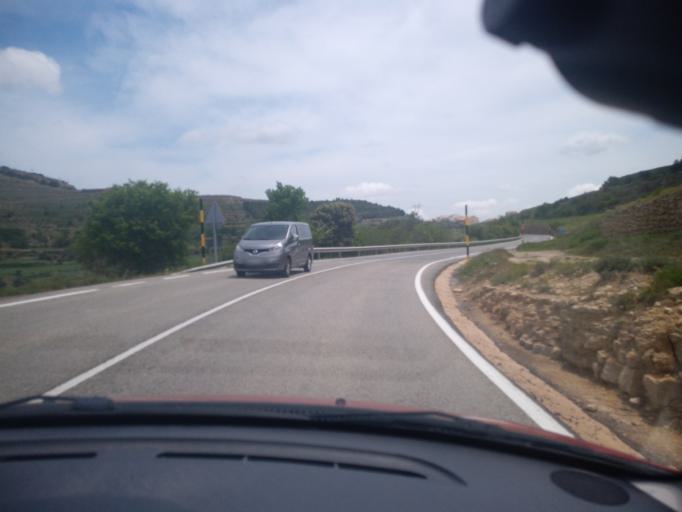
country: ES
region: Valencia
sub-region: Provincia de Castello
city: Ares del Maestre
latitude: 40.4579
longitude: -0.1476
